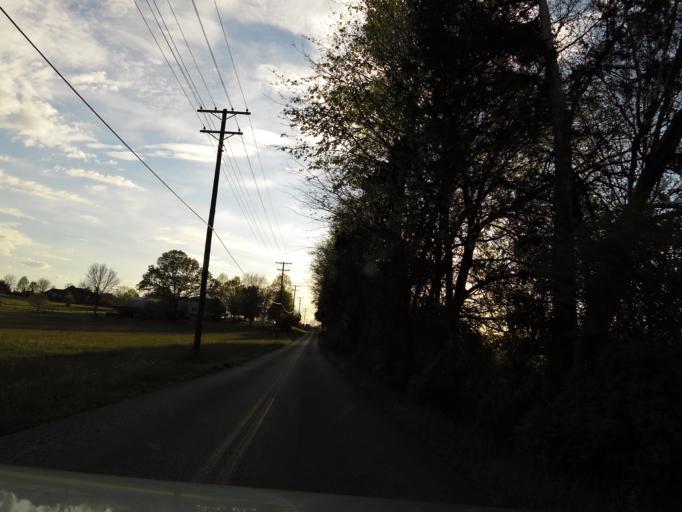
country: US
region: Tennessee
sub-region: Loudon County
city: Greenback
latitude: 35.6299
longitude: -84.0777
